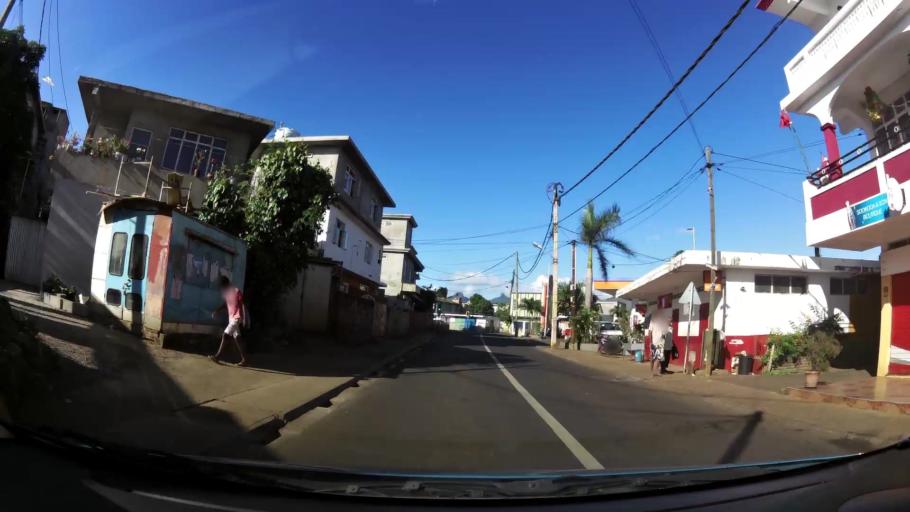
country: MU
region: Black River
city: Petite Riviere
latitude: -20.1966
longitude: 57.4449
